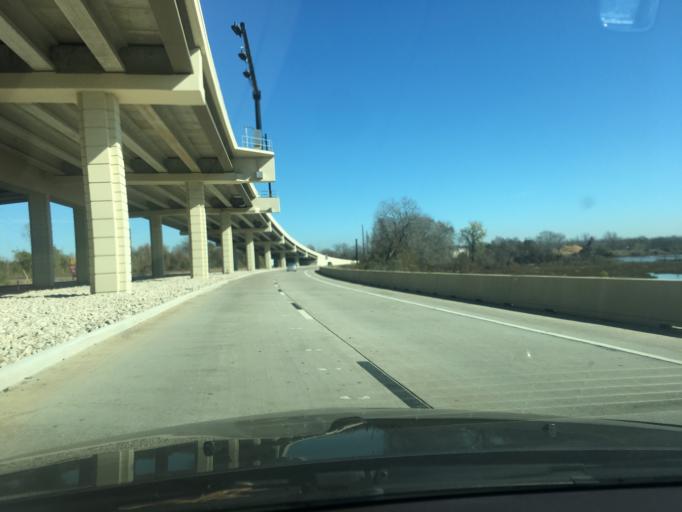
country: US
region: Texas
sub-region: Fort Bend County
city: Richmond
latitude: 29.5939
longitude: -95.7425
